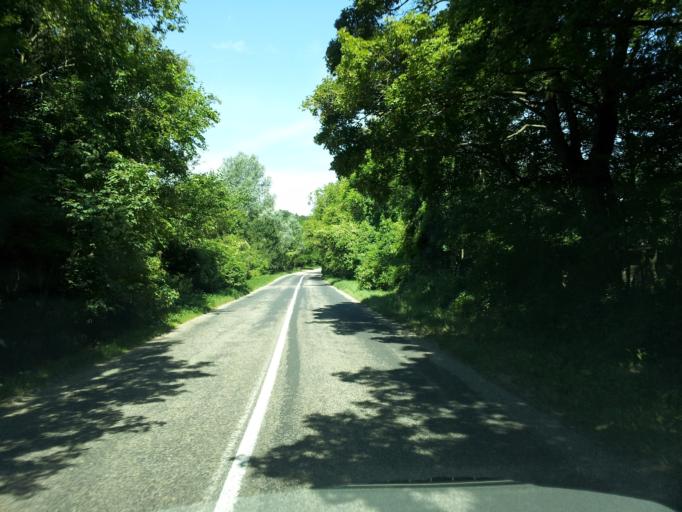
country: HU
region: Fejer
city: Szarliget
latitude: 47.5117
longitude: 18.5396
